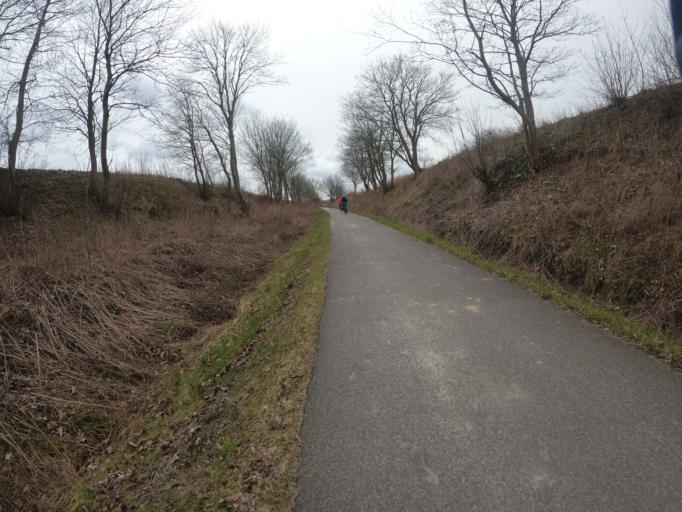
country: PL
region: West Pomeranian Voivodeship
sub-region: Powiat gryficki
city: Trzebiatow
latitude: 54.0796
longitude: 15.2600
